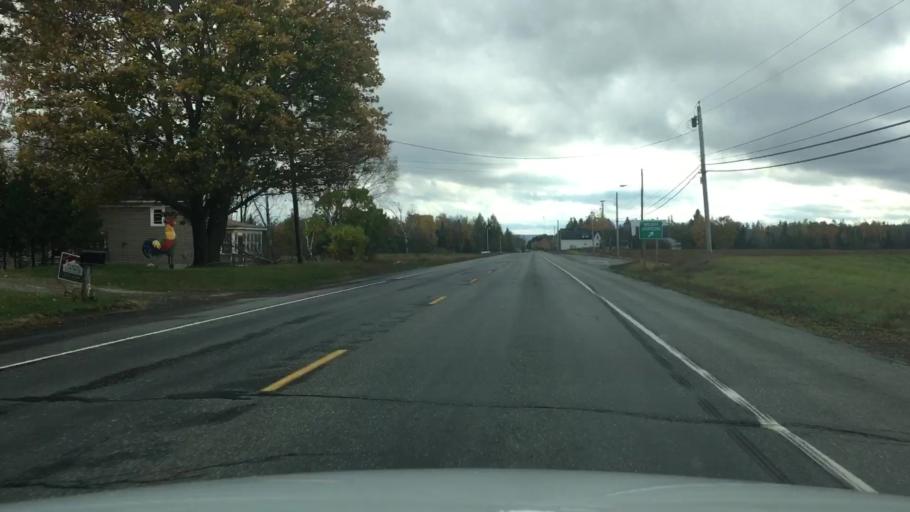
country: US
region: Maine
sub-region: Aroostook County
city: Houlton
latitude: 46.1807
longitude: -67.8411
